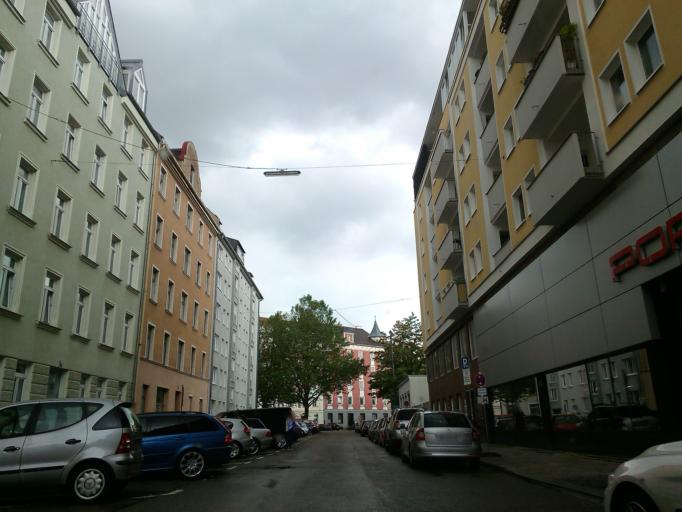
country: DE
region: Bavaria
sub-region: Upper Bavaria
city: Munich
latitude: 48.1290
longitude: 11.5919
